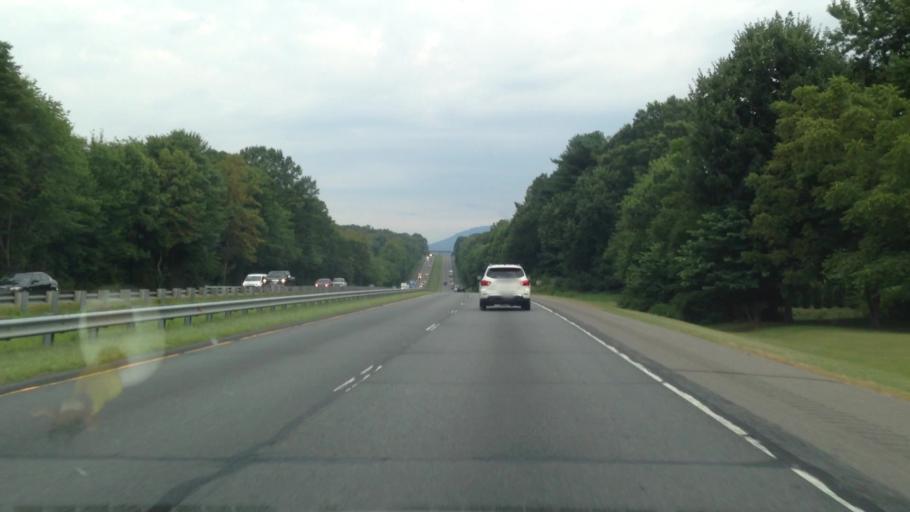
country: US
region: North Carolina
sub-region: Stokes County
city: King
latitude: 36.2765
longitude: -80.3813
